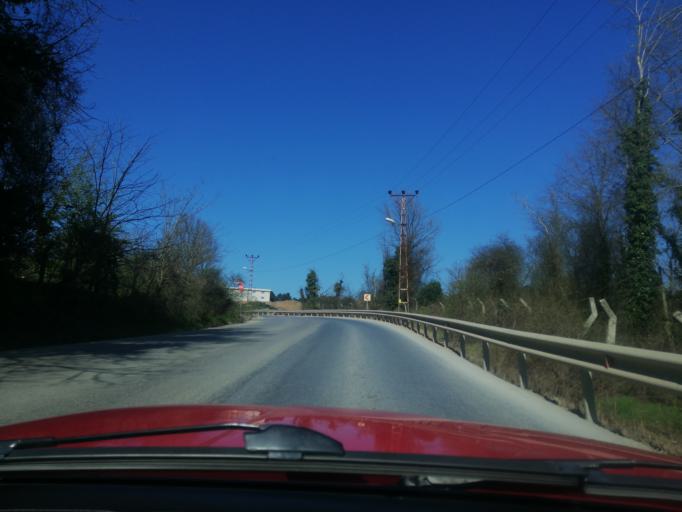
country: TR
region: Istanbul
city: Mahmut Sevket Pasa
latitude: 41.1052
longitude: 29.1600
